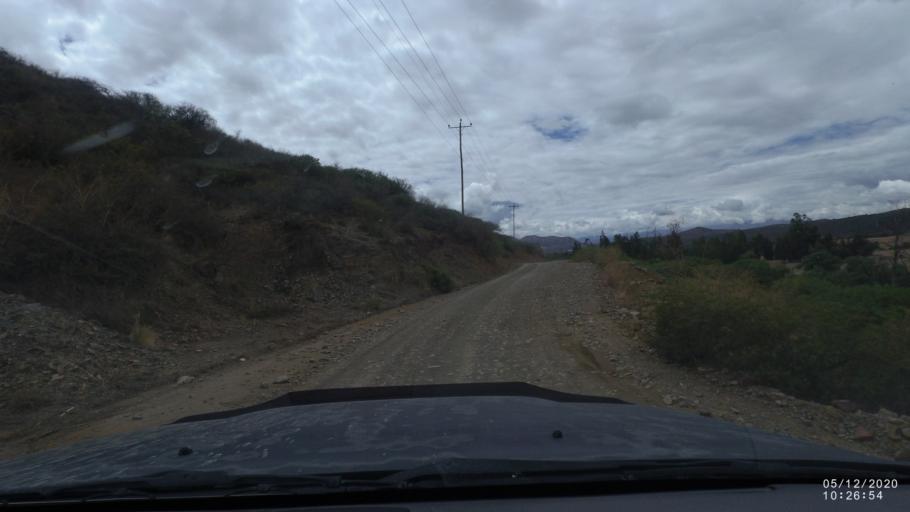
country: BO
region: Cochabamba
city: Sipe Sipe
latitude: -17.5291
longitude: -66.2806
